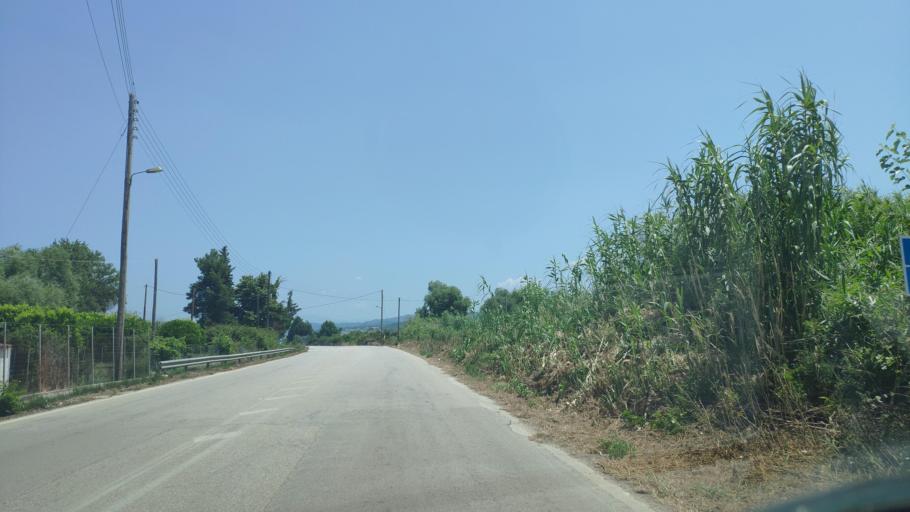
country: GR
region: Epirus
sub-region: Nomos Artas
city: Kostakioi
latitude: 39.1205
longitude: 20.9362
